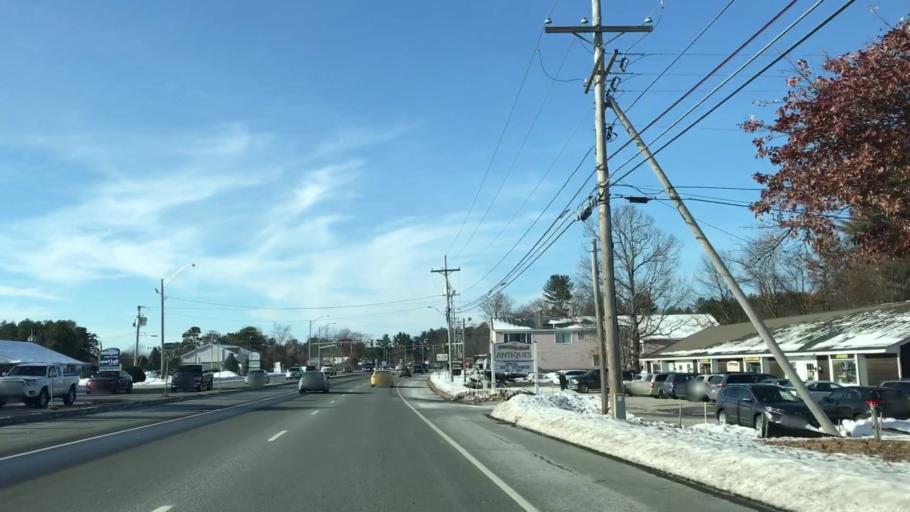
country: US
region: New Hampshire
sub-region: Hillsborough County
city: Hollis
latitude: 42.8085
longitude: -71.5711
